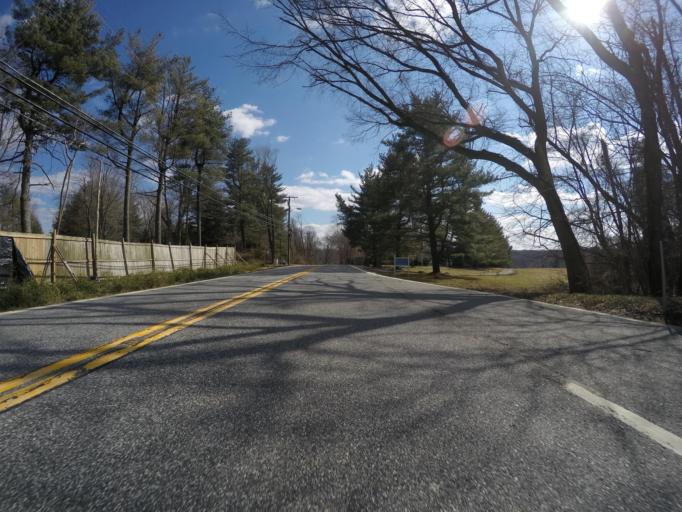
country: US
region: Maryland
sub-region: Baltimore County
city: Mays Chapel
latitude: 39.4505
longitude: -76.6866
